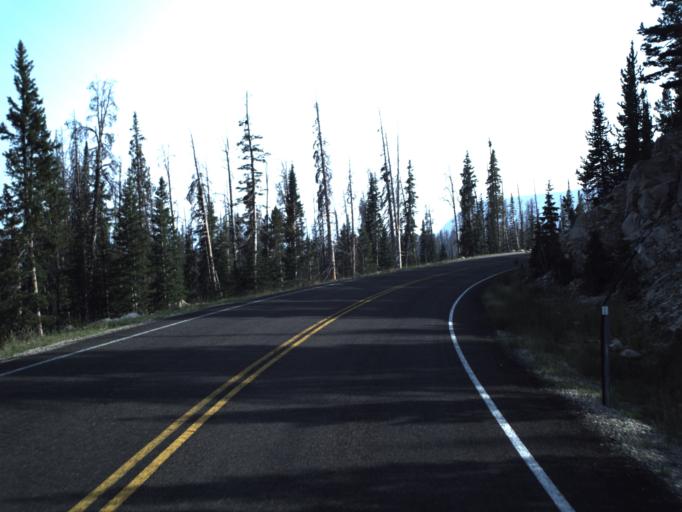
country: US
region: Utah
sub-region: Summit County
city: Kamas
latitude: 40.7144
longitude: -110.8759
